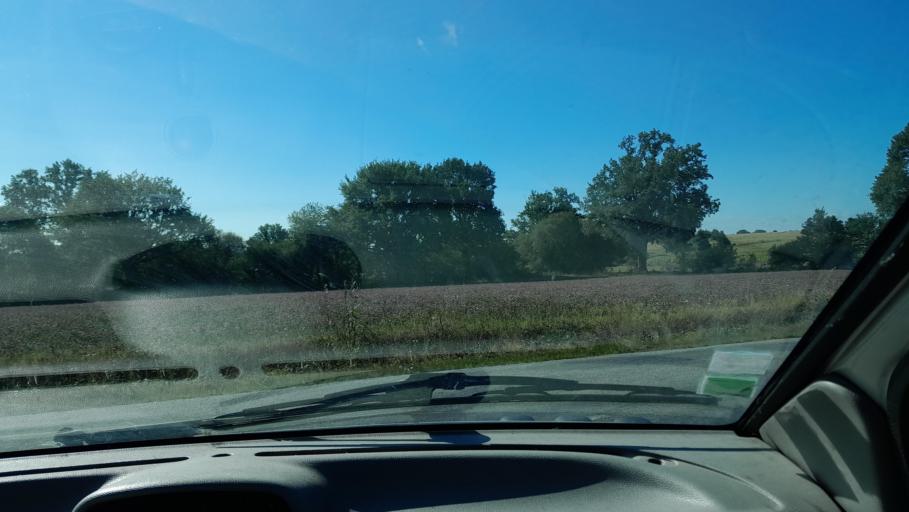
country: FR
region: Pays de la Loire
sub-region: Departement de la Mayenne
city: Ballots
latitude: 47.9580
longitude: -1.0563
